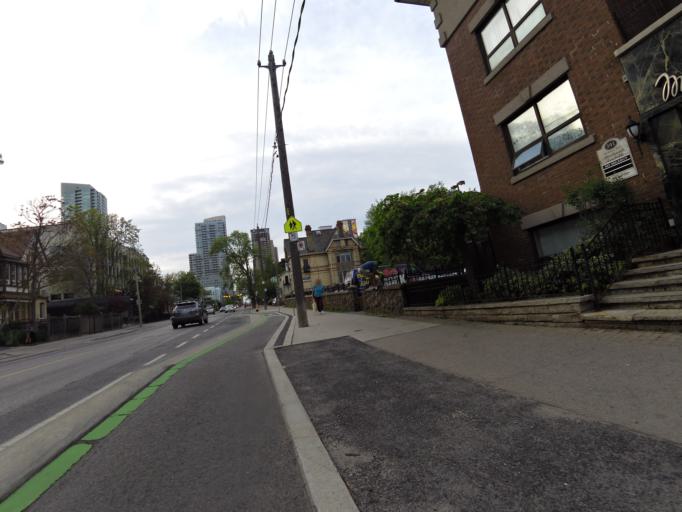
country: CA
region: Ontario
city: Toronto
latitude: 43.6642
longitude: -79.3734
